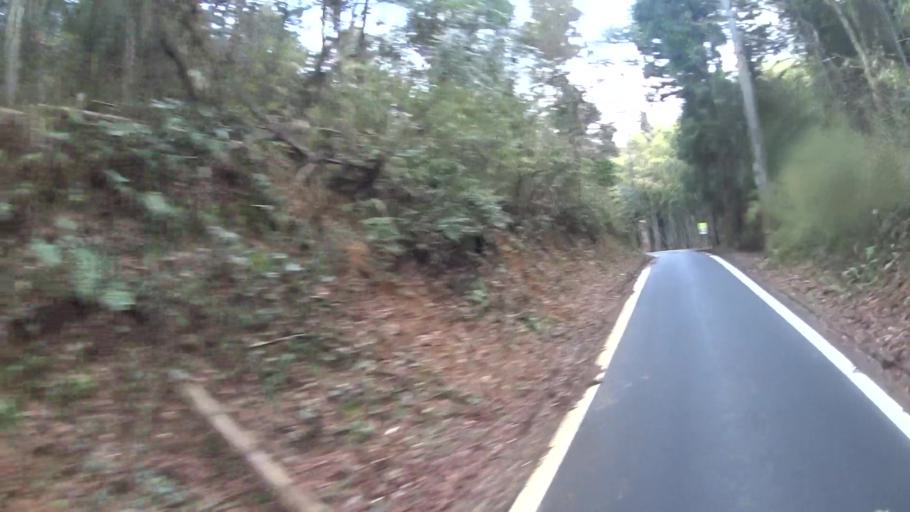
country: JP
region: Kyoto
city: Maizuru
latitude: 35.4368
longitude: 135.2985
